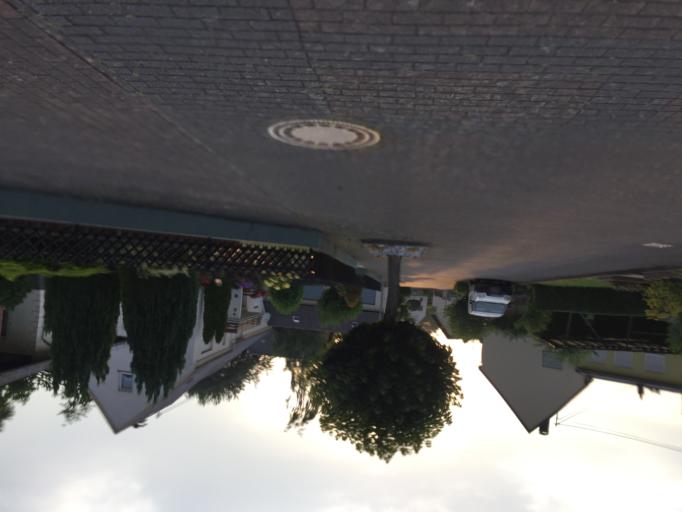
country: DE
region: Rheinland-Pfalz
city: Weroth
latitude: 50.4604
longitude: 7.9481
